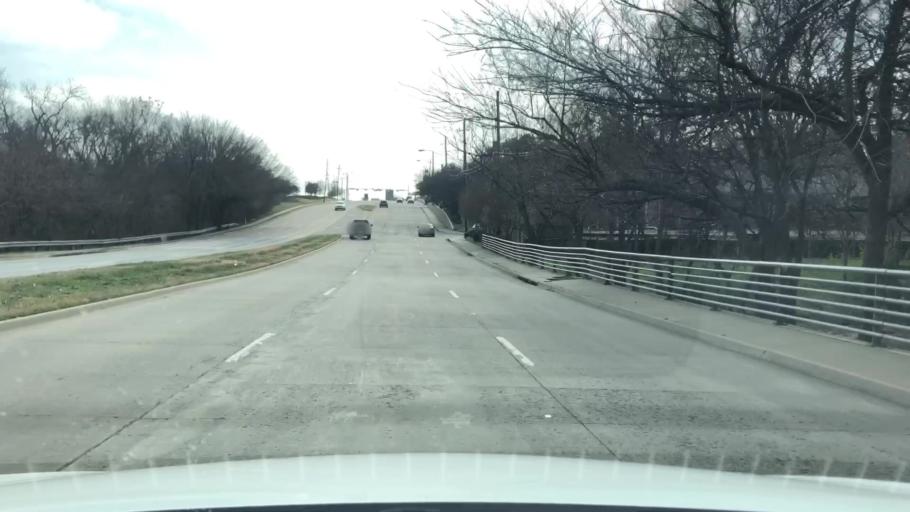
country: US
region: Texas
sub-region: Dallas County
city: Addison
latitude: 33.0063
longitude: -96.8574
